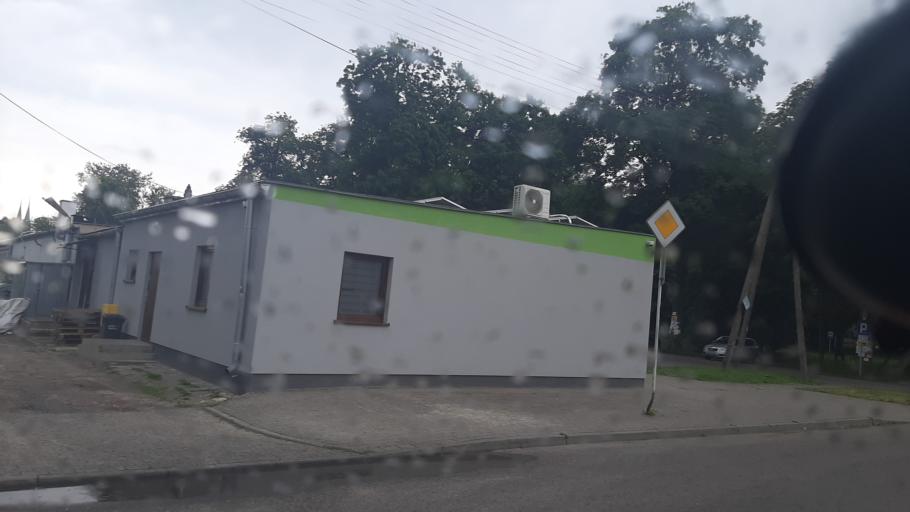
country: PL
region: Lublin Voivodeship
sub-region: Powiat lubelski
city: Garbow
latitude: 51.3549
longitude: 22.3341
